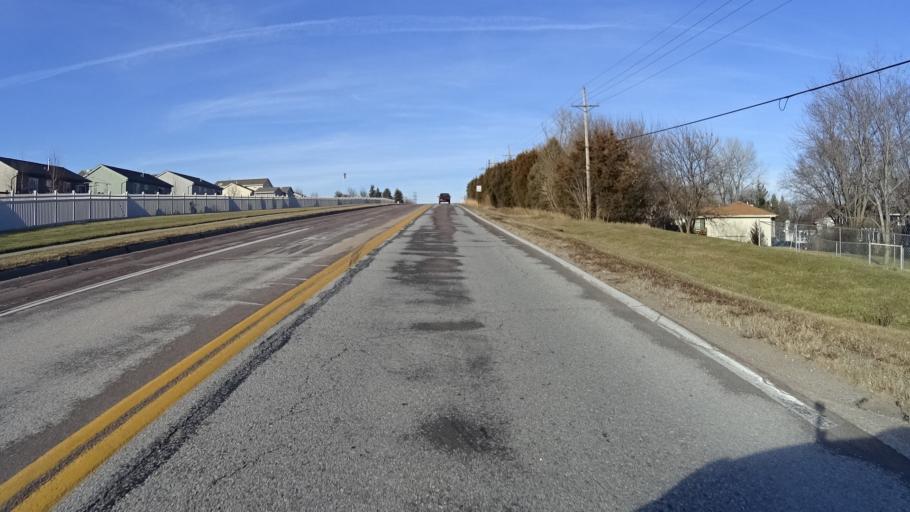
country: US
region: Nebraska
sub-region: Sarpy County
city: Offutt Air Force Base
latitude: 41.1525
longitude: -95.9476
